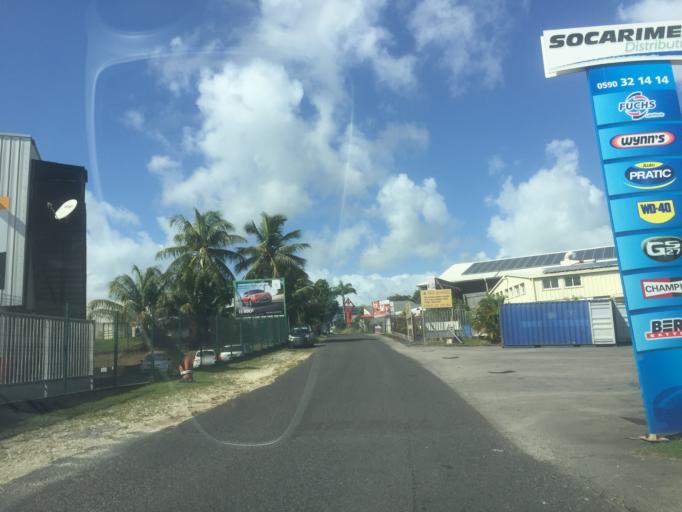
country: GP
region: Guadeloupe
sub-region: Guadeloupe
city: Baie-Mahault
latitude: 16.2417
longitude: -61.5811
